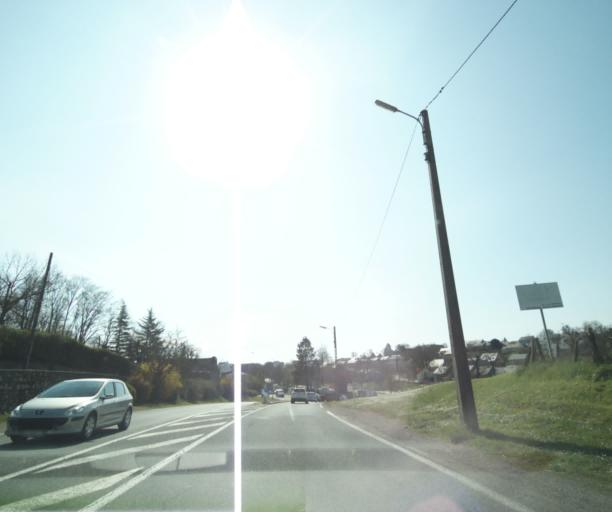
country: FR
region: Midi-Pyrenees
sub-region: Departement de l'Aveyron
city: Olemps
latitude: 44.3653
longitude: 2.5512
